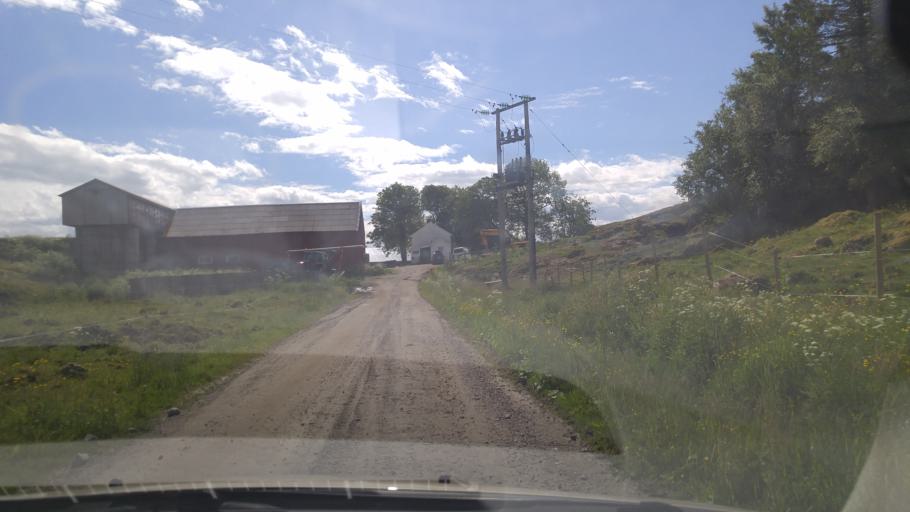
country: NO
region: Nord-Trondelag
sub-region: Vikna
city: Rorvik
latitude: 64.8942
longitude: 11.1082
